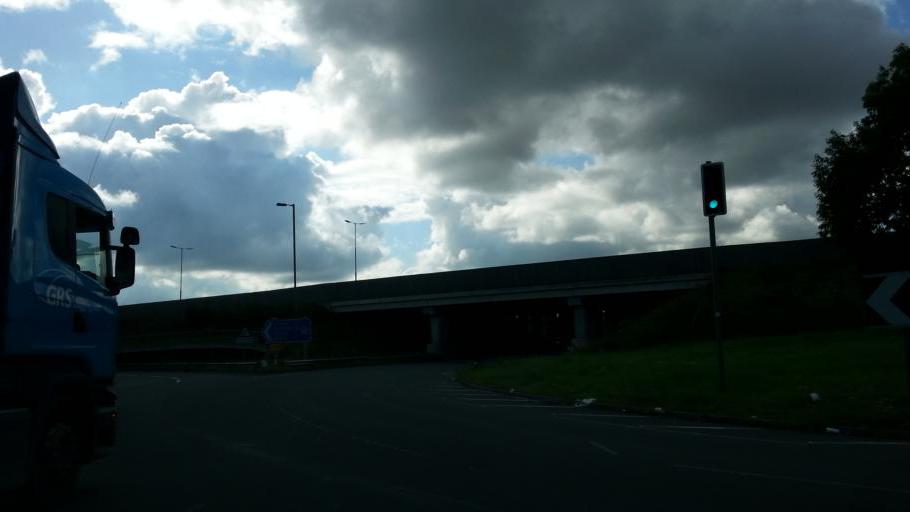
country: GB
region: England
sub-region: West Berkshire
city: Eton
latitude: 51.5037
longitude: -0.6157
